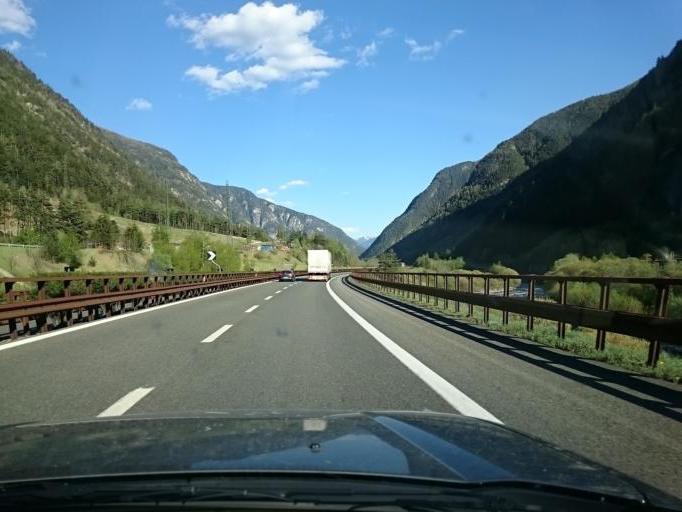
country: IT
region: Trentino-Alto Adige
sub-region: Bolzano
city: Fortezza
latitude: 46.8124
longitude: 11.5578
